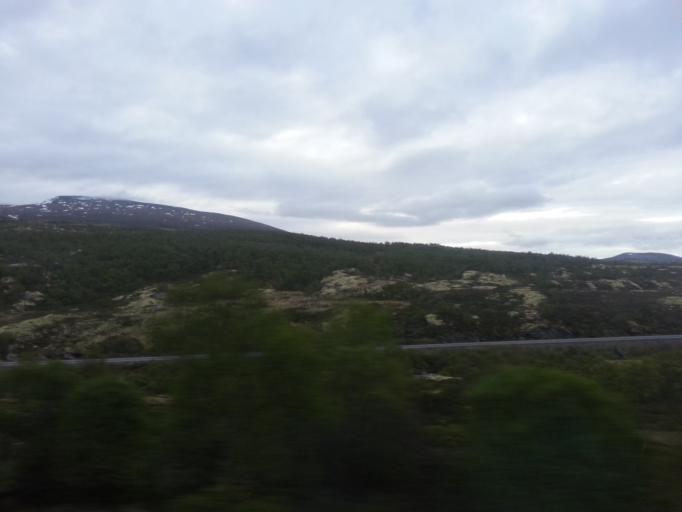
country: NO
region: Sor-Trondelag
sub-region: Oppdal
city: Oppdal
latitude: 62.2857
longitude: 9.5961
